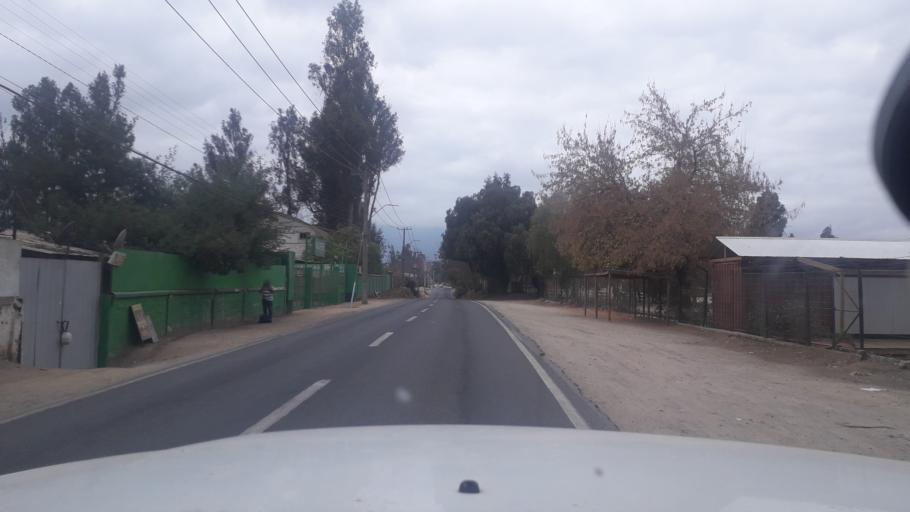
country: CL
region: Valparaiso
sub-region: Provincia de Marga Marga
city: Limache
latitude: -33.0183
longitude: -71.2718
